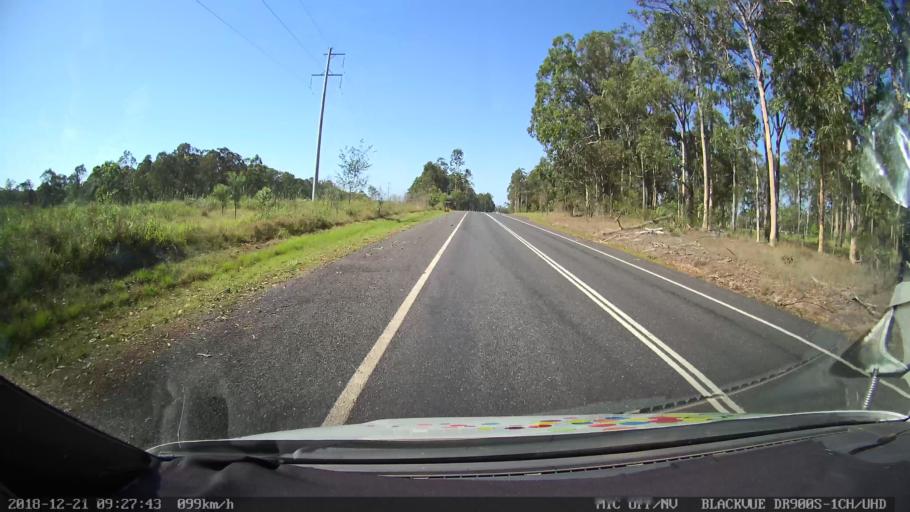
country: AU
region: New South Wales
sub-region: Clarence Valley
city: Maclean
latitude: -29.4068
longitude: 152.9889
